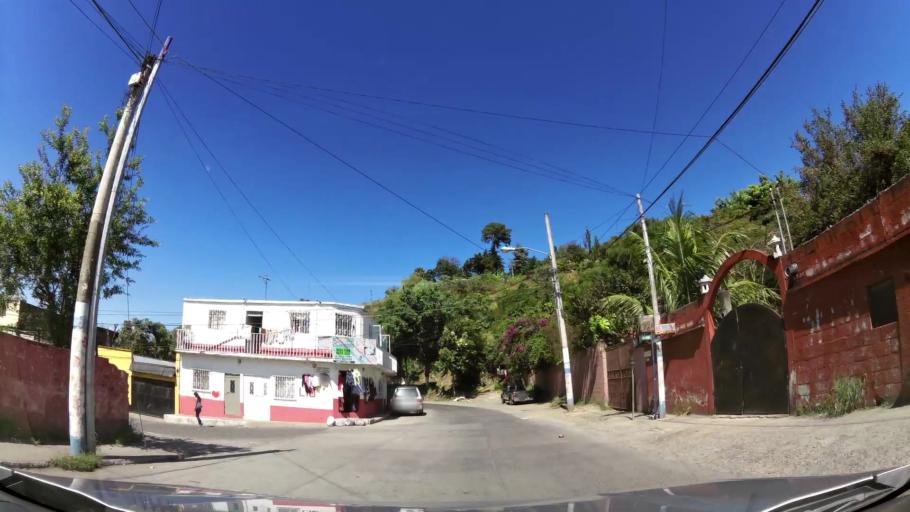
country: GT
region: Guatemala
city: Villa Canales
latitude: 14.4860
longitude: -90.5333
